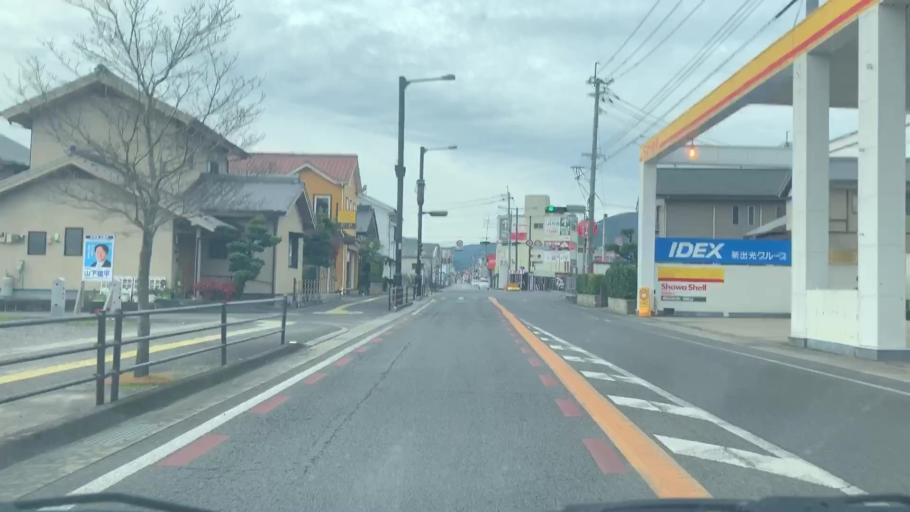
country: JP
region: Saga Prefecture
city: Ureshinomachi-shimojuku
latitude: 33.1020
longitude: 129.9919
